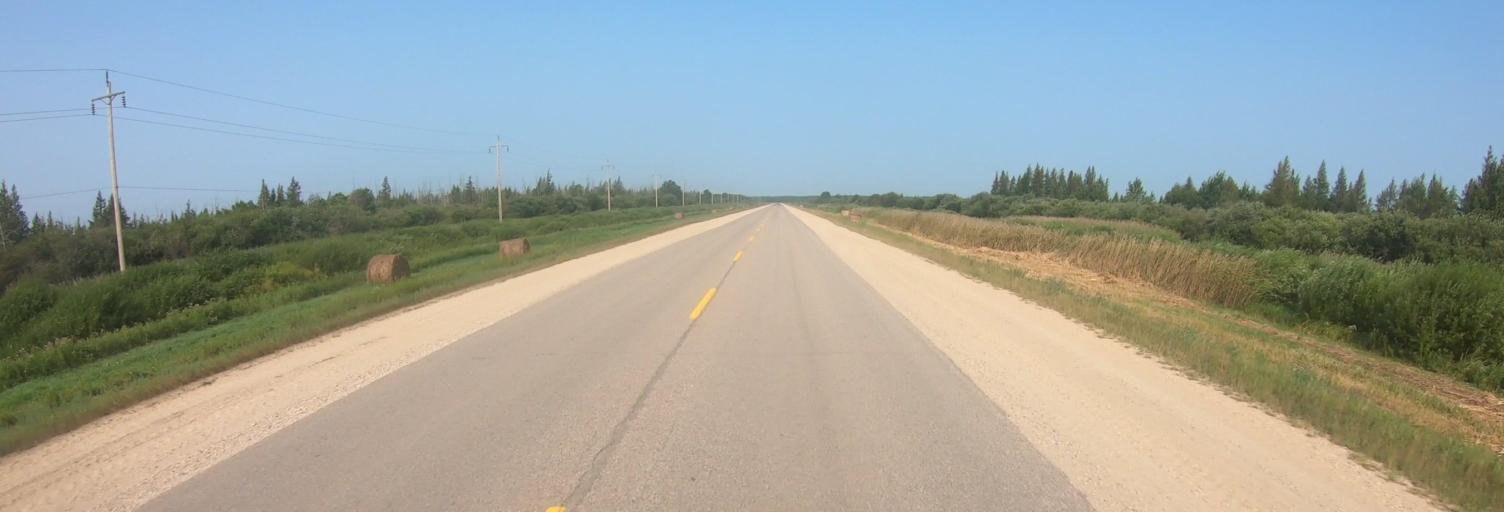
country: US
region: Minnesota
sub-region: Roseau County
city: Warroad
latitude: 49.0173
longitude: -95.5420
